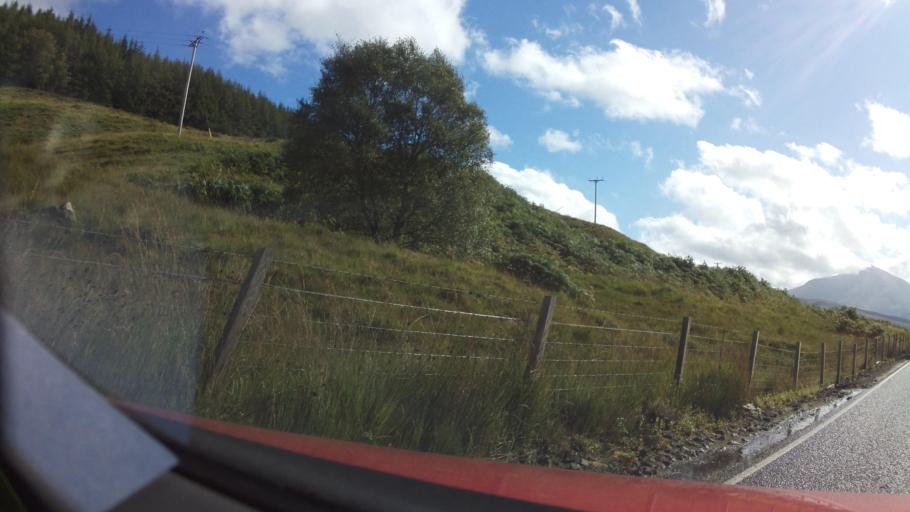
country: GB
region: Scotland
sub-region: Argyll and Bute
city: Garelochhead
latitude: 56.4300
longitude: -4.7005
